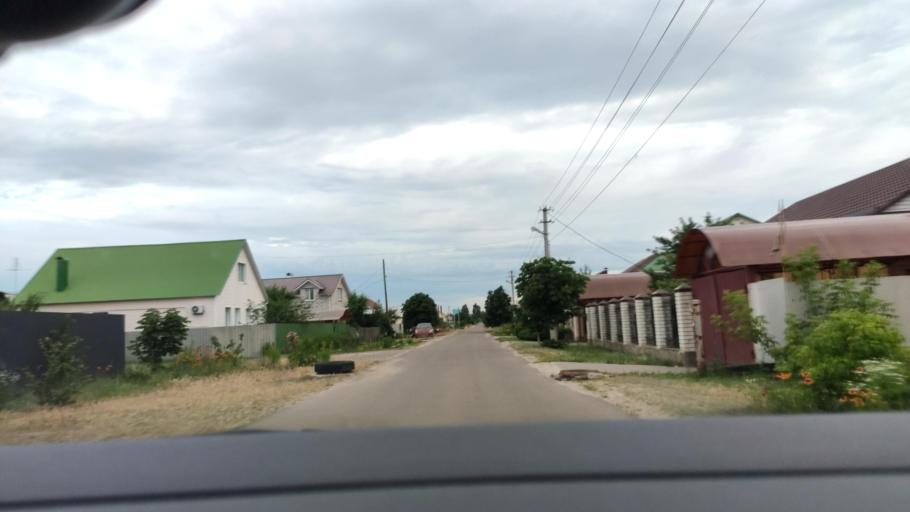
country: RU
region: Voronezj
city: Maslovka
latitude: 51.5722
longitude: 39.2507
